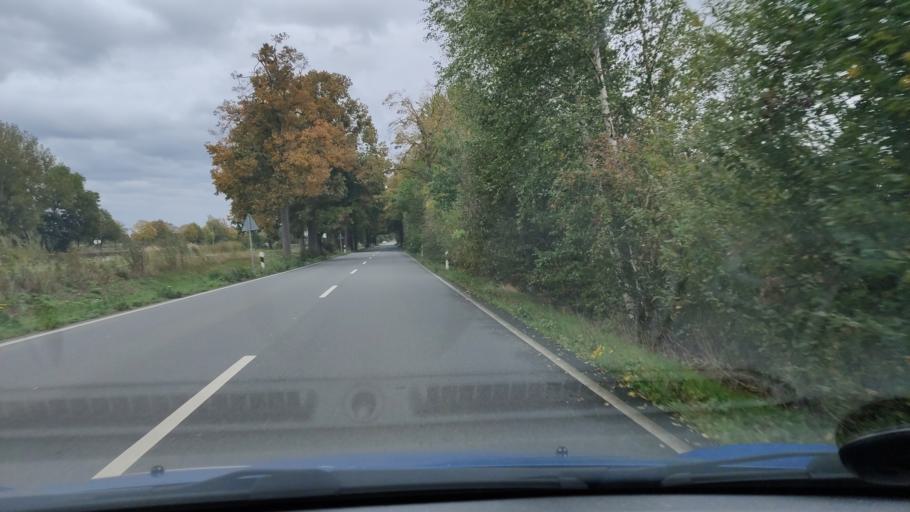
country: DE
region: Lower Saxony
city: Garbsen
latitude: 52.4001
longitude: 9.5405
